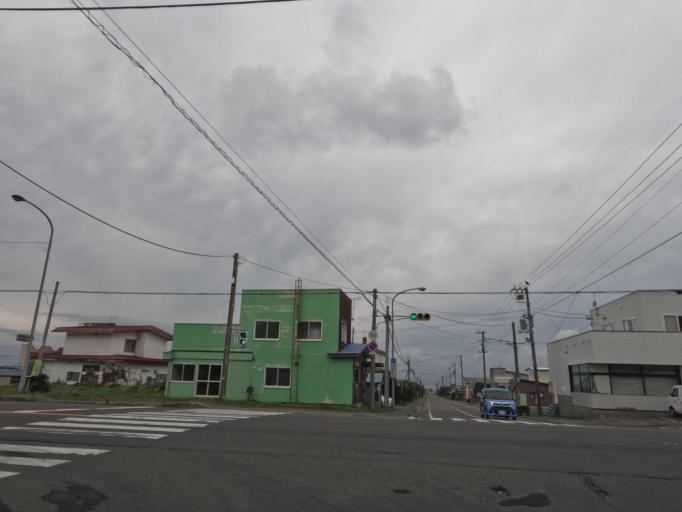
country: JP
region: Hokkaido
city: Date
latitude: 42.4279
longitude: 140.9051
